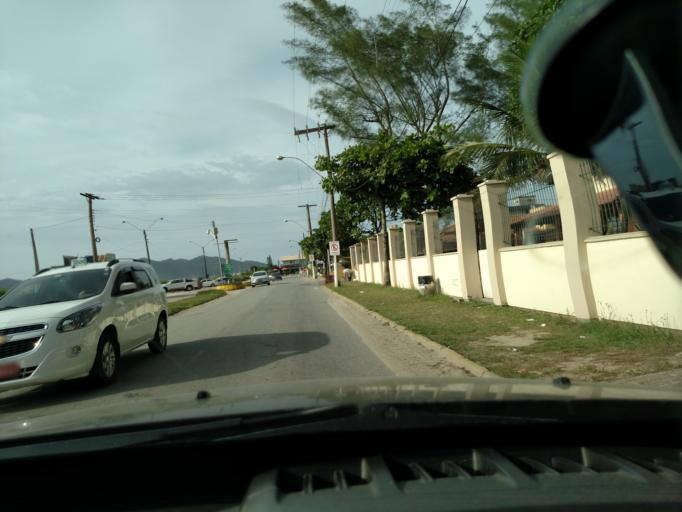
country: BR
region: Santa Catarina
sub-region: Porto Belo
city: Porto Belo
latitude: -27.1693
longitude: -48.4990
